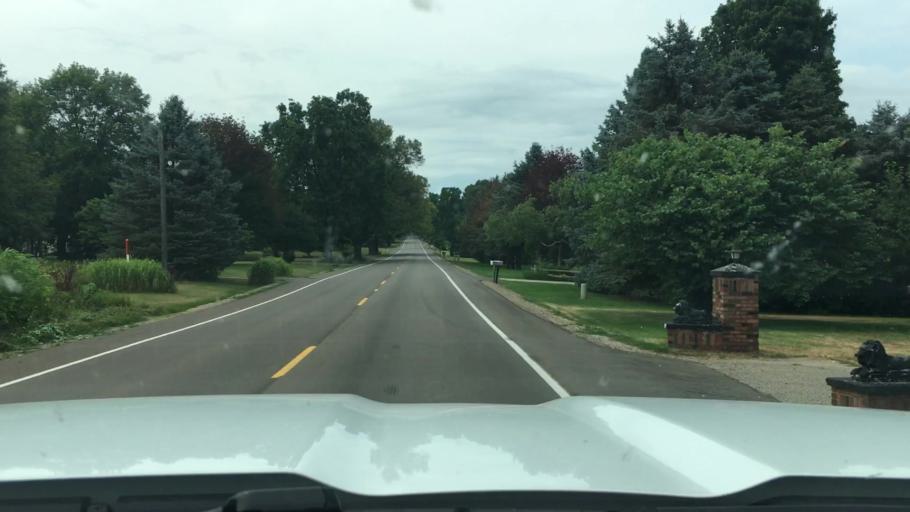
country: US
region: Michigan
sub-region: Allegan County
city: Plainwell
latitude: 42.4601
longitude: -85.6027
